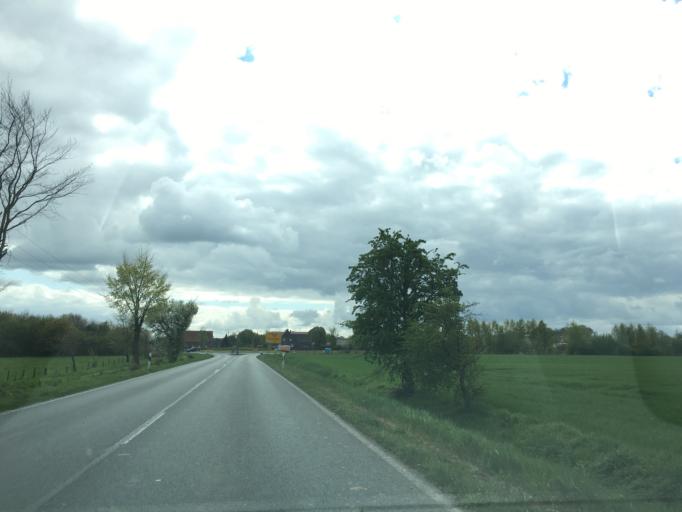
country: DE
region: North Rhine-Westphalia
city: Ludinghausen
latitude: 51.7706
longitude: 7.3862
